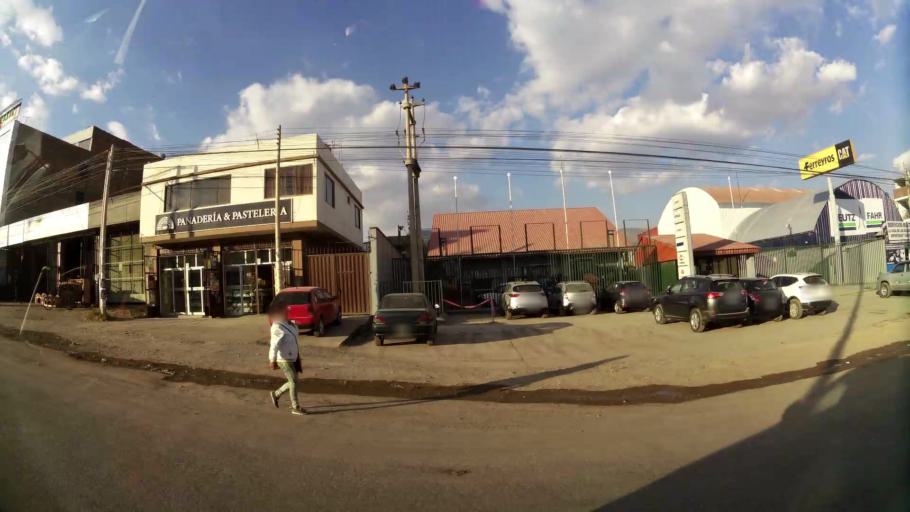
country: PE
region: Junin
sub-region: Provincia de Huancayo
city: Pilcomay
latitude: -12.0402
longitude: -75.2281
